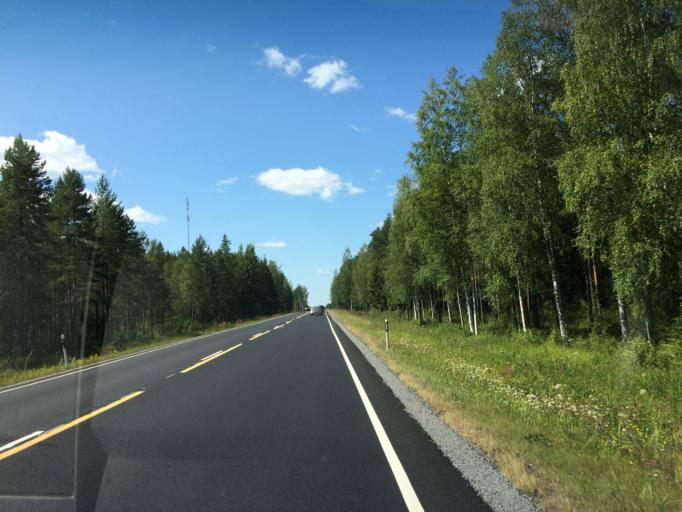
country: FI
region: Pirkanmaa
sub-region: Lounais-Pirkanmaa
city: Kiikoinen
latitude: 61.4747
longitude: 22.4793
